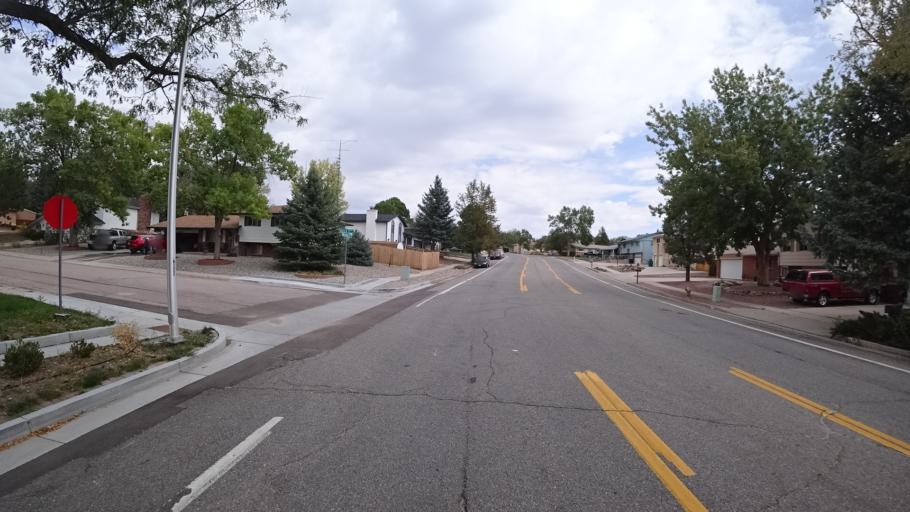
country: US
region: Colorado
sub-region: El Paso County
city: Cimarron Hills
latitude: 38.8532
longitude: -104.7380
